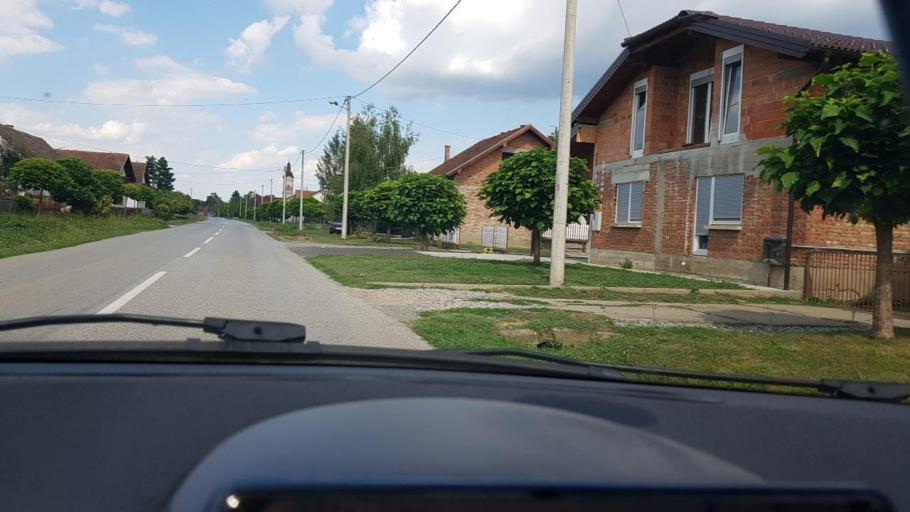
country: HR
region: Bjelovarsko-Bilogorska
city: Zdralovi
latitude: 45.8376
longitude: 16.9632
